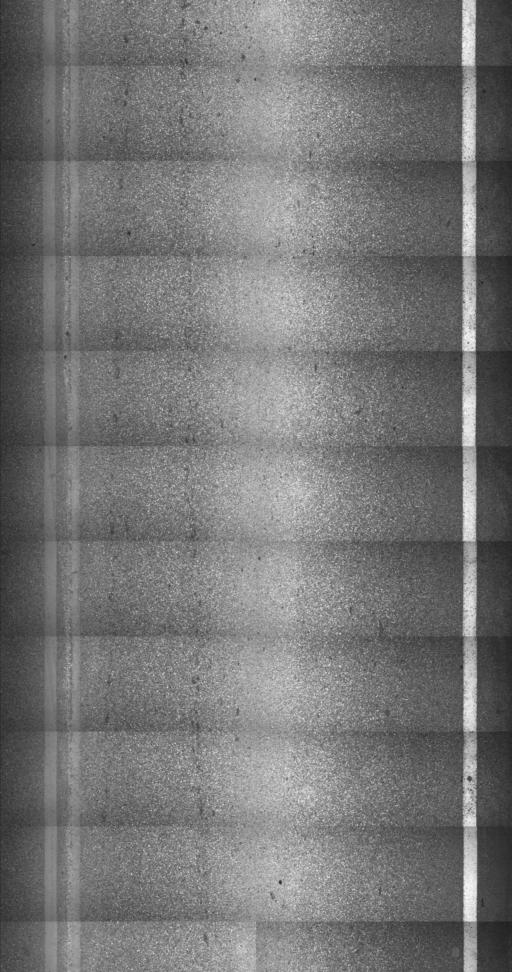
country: US
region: Vermont
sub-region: Franklin County
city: Swanton
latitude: 44.9406
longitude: -73.0372
